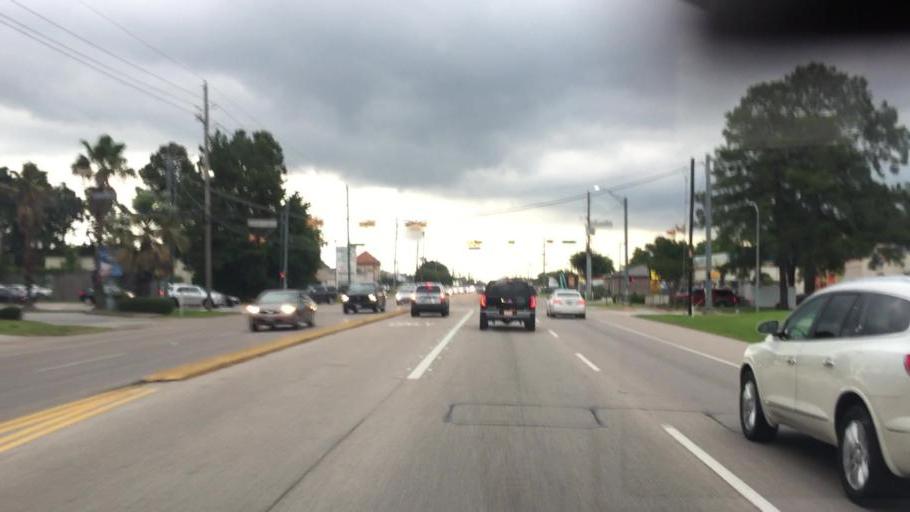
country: US
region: Texas
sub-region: Harris County
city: Spring
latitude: 30.0360
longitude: -95.4966
